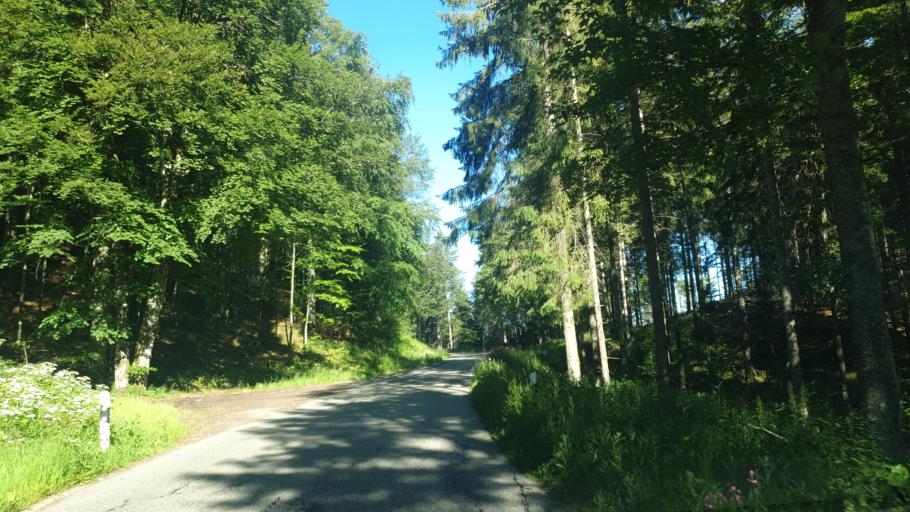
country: DE
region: Baden-Wuerttemberg
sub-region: Freiburg Region
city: Horben
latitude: 47.9072
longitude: 7.8830
